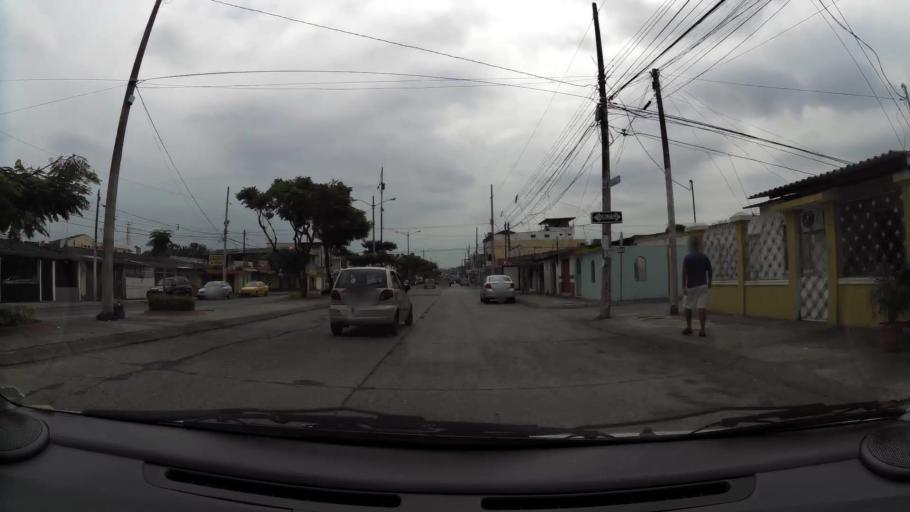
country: EC
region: Guayas
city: Eloy Alfaro
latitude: -2.1212
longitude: -79.8977
